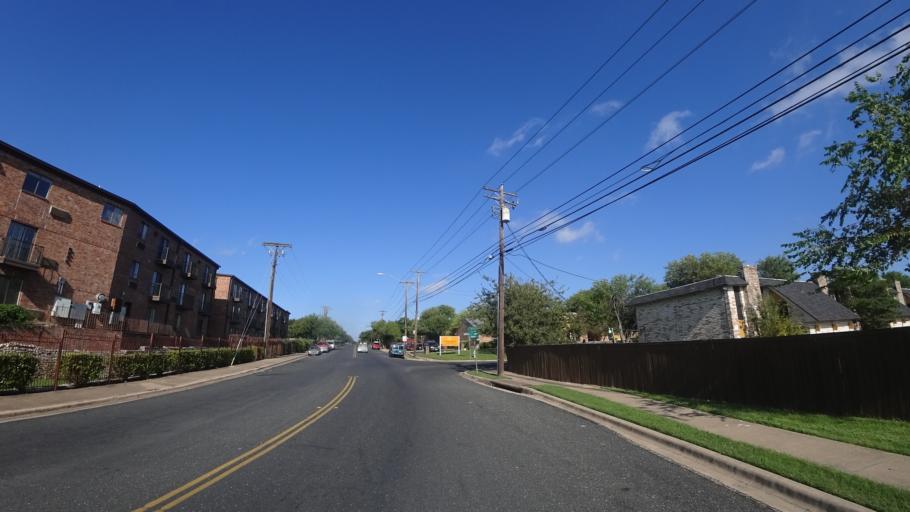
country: US
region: Texas
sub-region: Travis County
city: Austin
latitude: 30.3248
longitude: -97.6955
